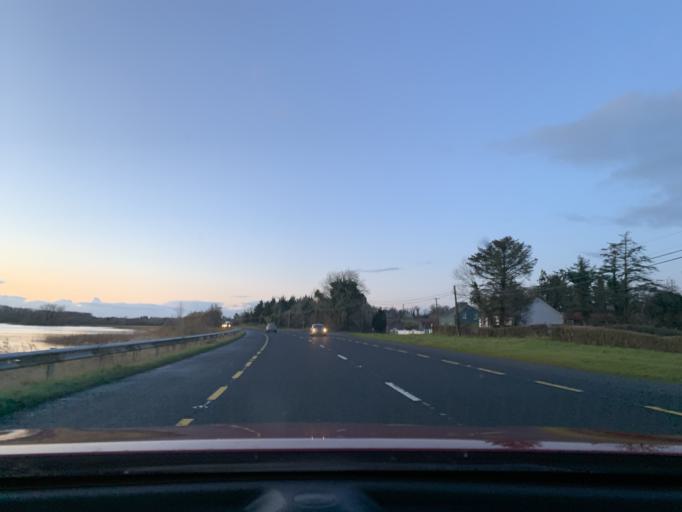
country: IE
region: Connaught
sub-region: County Leitrim
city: Carrick-on-Shannon
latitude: 53.9129
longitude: -7.9688
